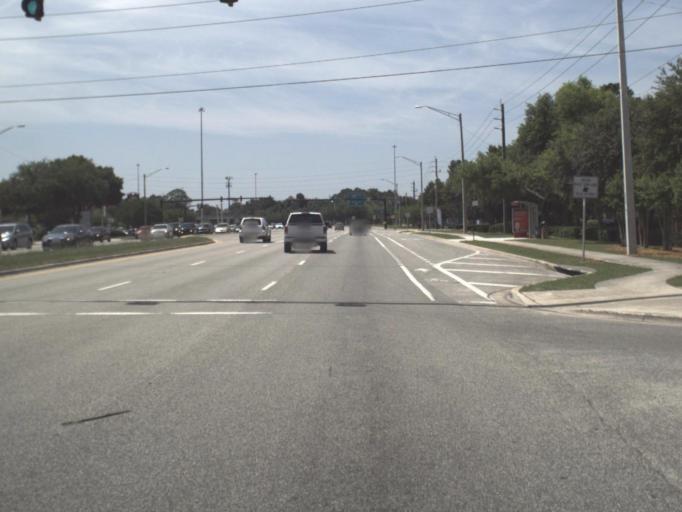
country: US
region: Florida
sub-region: Saint Johns County
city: Fruit Cove
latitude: 30.1874
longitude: -81.6279
